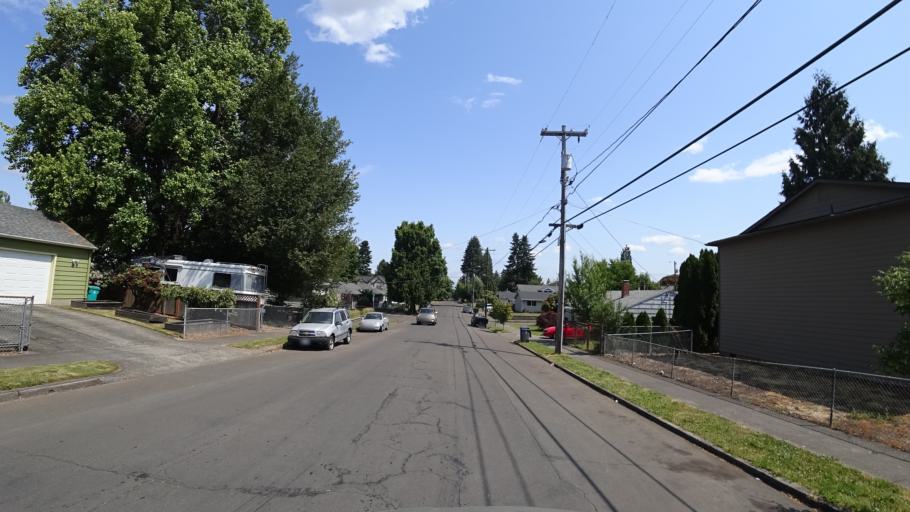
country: US
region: Oregon
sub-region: Washington County
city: West Haven
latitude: 45.5967
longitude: -122.7479
